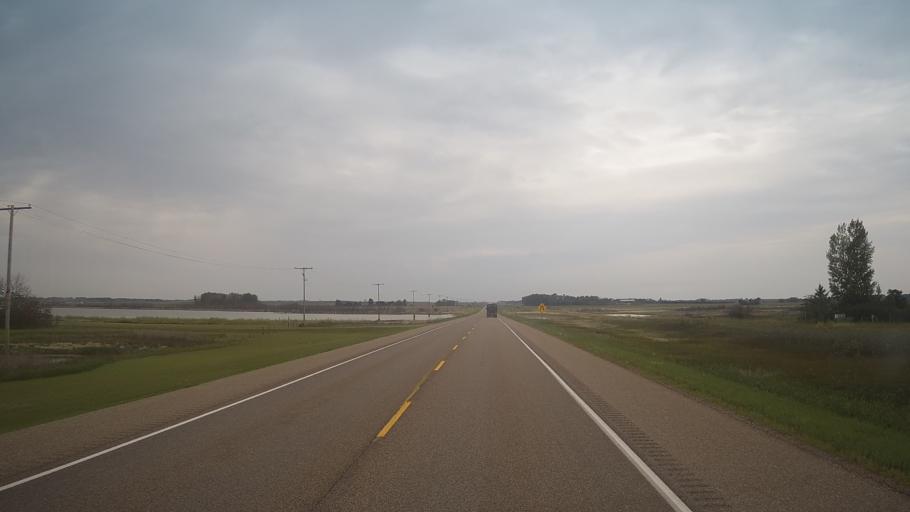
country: CA
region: Saskatchewan
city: Langham
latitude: 52.1289
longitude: -107.1254
